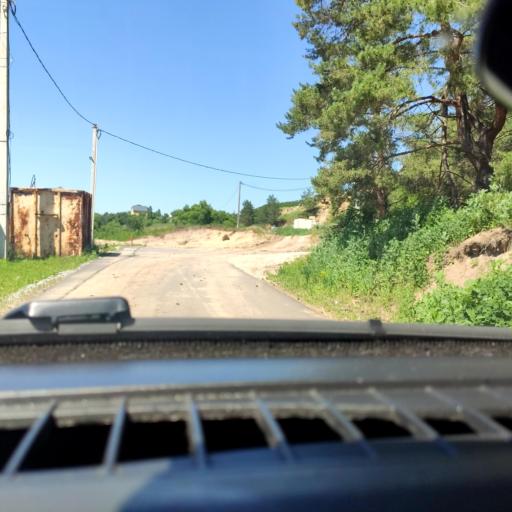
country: RU
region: Voronezj
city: Podgornoye
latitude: 51.7967
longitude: 39.1358
